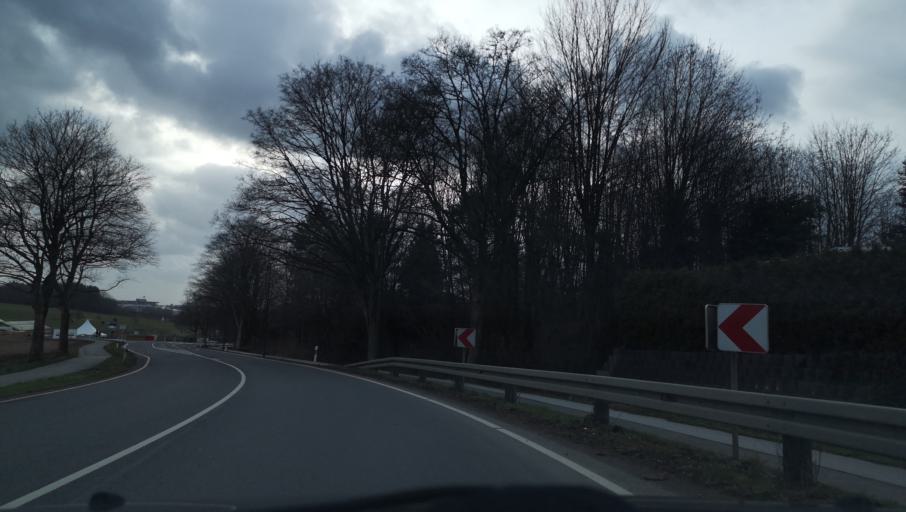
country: DE
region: North Rhine-Westphalia
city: Huckeswagen
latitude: 51.1473
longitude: 7.3106
